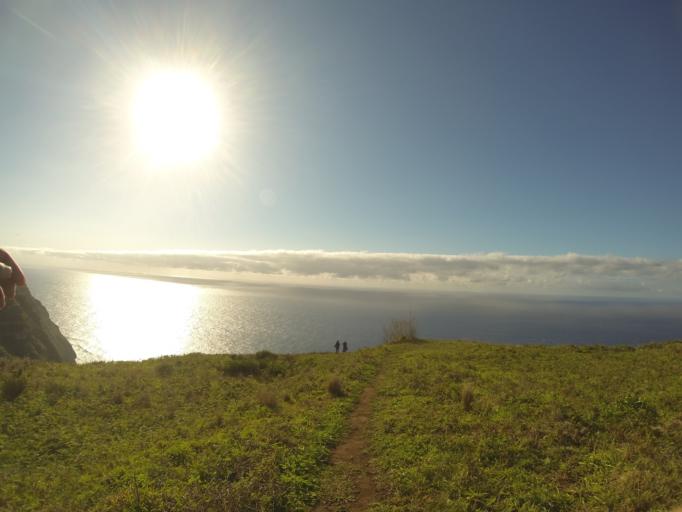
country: PT
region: Madeira
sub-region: Calheta
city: Faja da Ovelha
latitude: 32.8203
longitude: -17.2518
